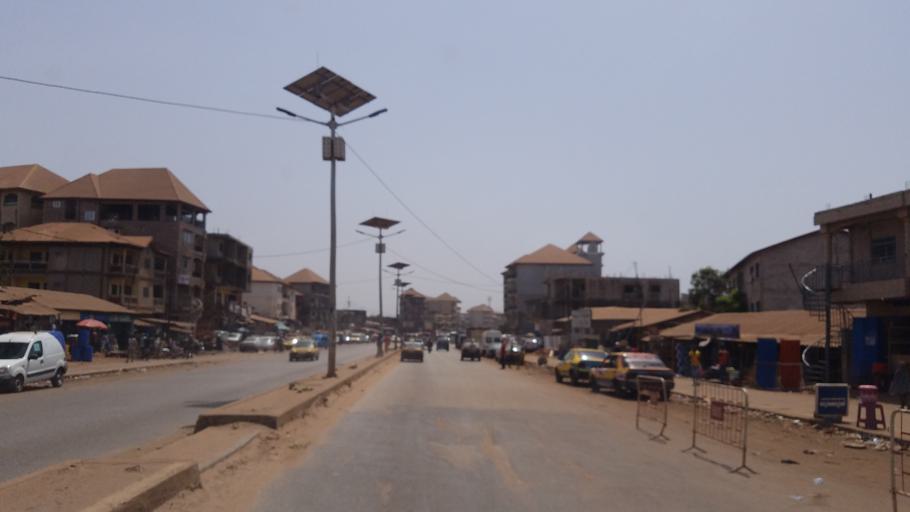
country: GN
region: Kindia
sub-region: Prefecture de Dubreka
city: Dubreka
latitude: 9.6686
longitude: -13.5586
